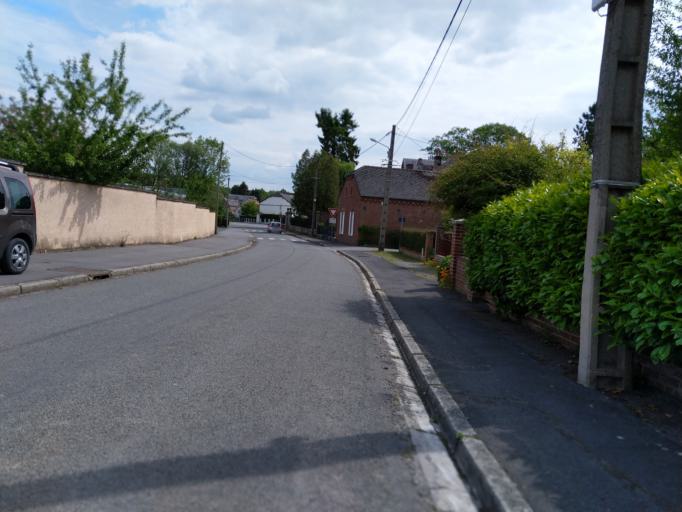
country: FR
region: Picardie
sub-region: Departement de l'Aisne
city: Boue
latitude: 50.0118
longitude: 3.6953
